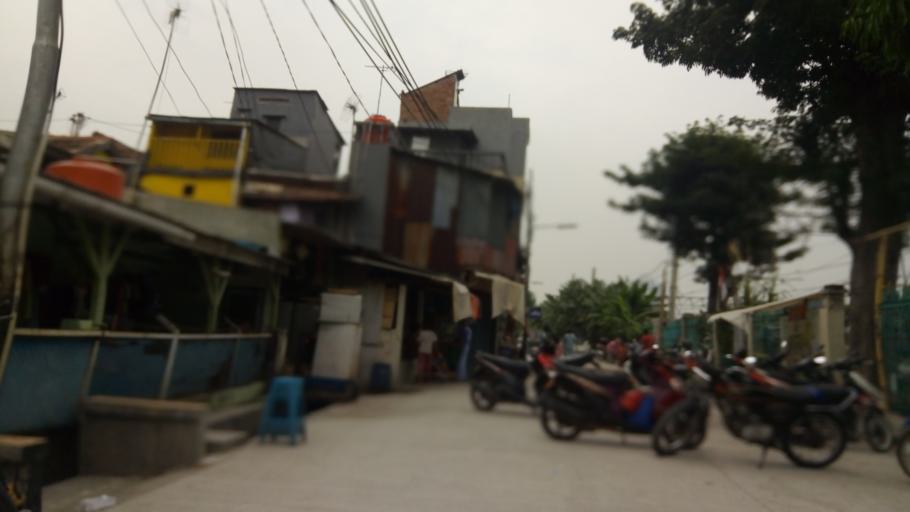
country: ID
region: Jakarta Raya
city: Jakarta
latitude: -6.1551
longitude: 106.8395
